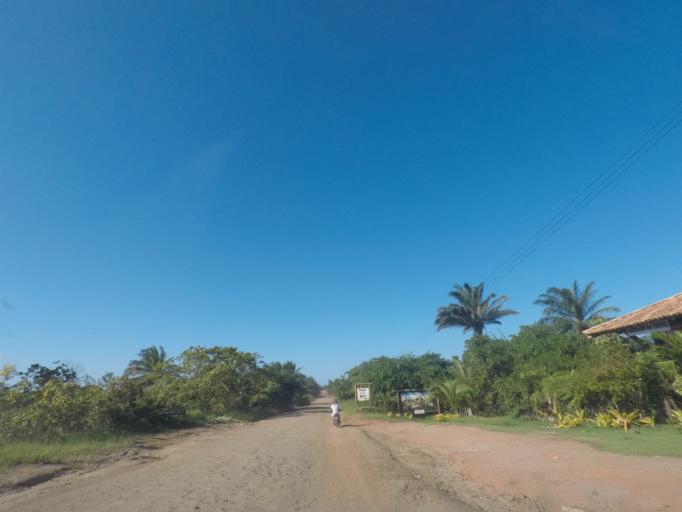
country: BR
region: Bahia
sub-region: Marau
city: Marau
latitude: -14.0355
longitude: -38.9548
